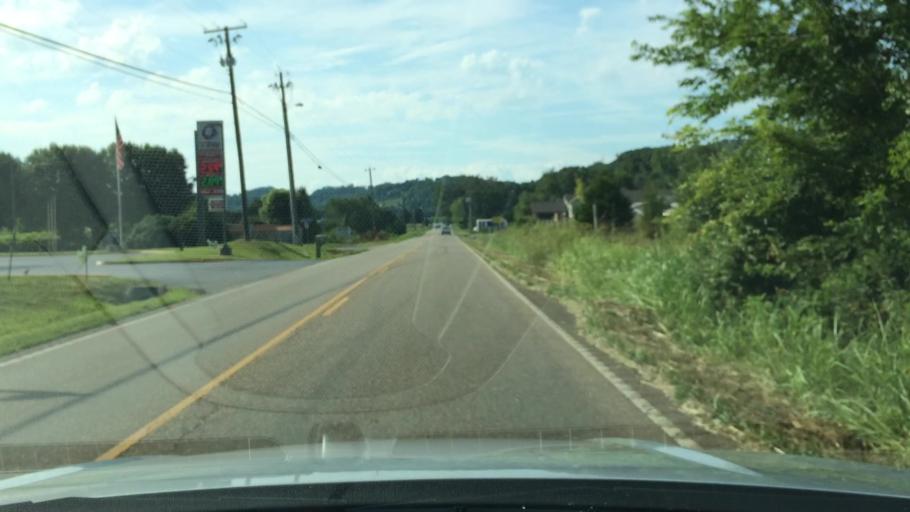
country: US
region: Tennessee
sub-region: Sevier County
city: Seymour
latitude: 35.9216
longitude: -83.6470
